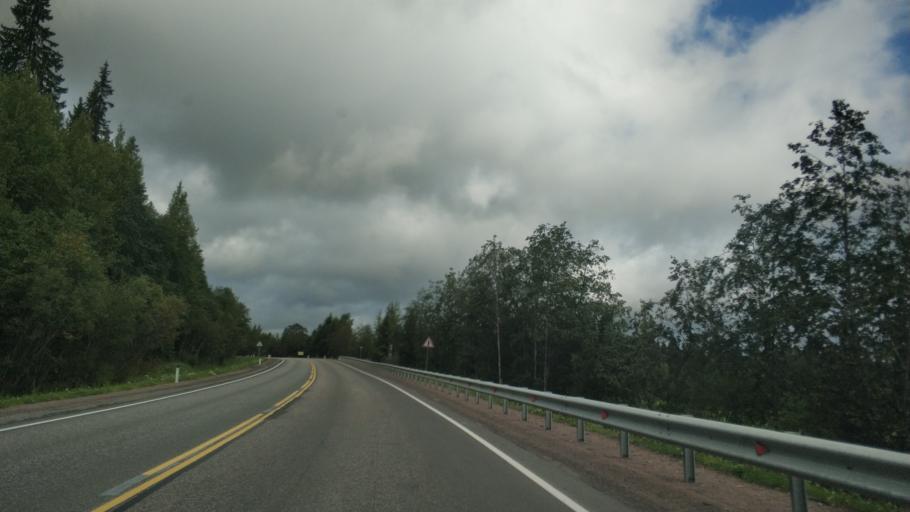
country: RU
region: Republic of Karelia
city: Khelyulya
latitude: 61.7833
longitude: 30.6558
